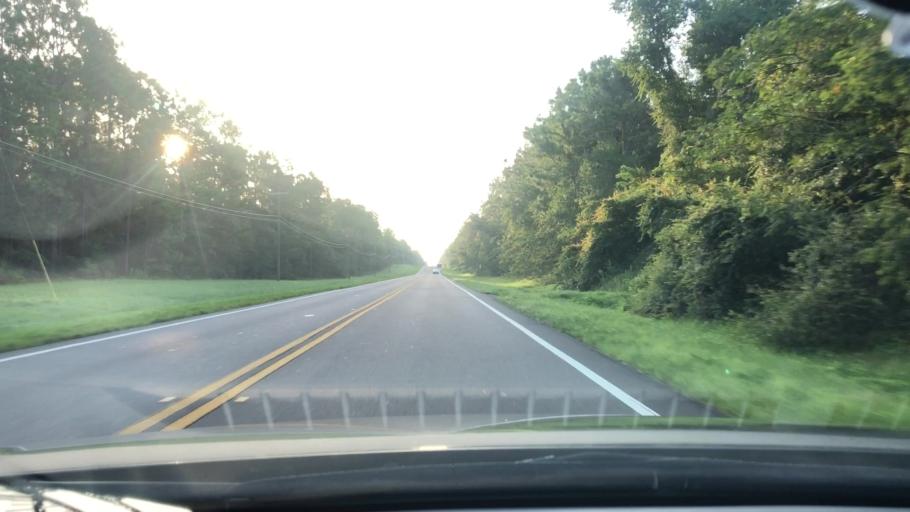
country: US
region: Florida
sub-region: Marion County
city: Belleview
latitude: 29.0262
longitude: -82.2364
